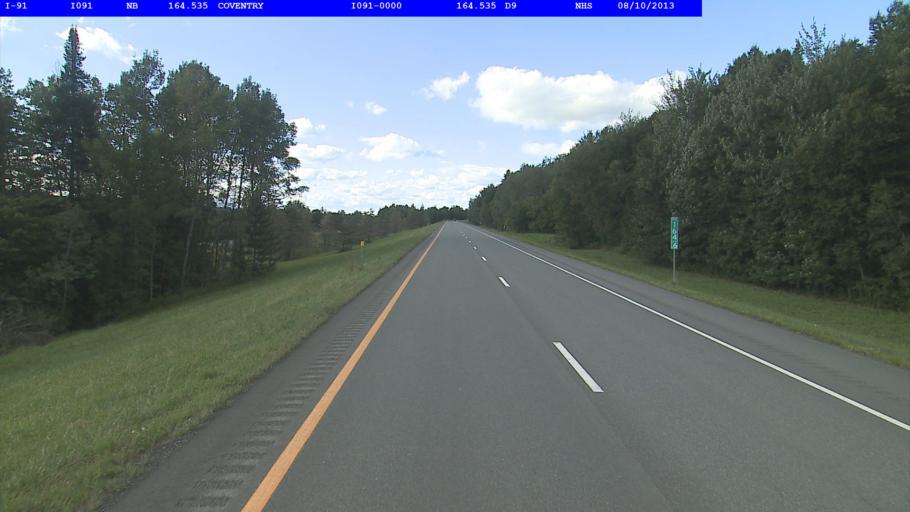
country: US
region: Vermont
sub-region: Orleans County
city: Newport
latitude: 44.8482
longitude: -72.1930
